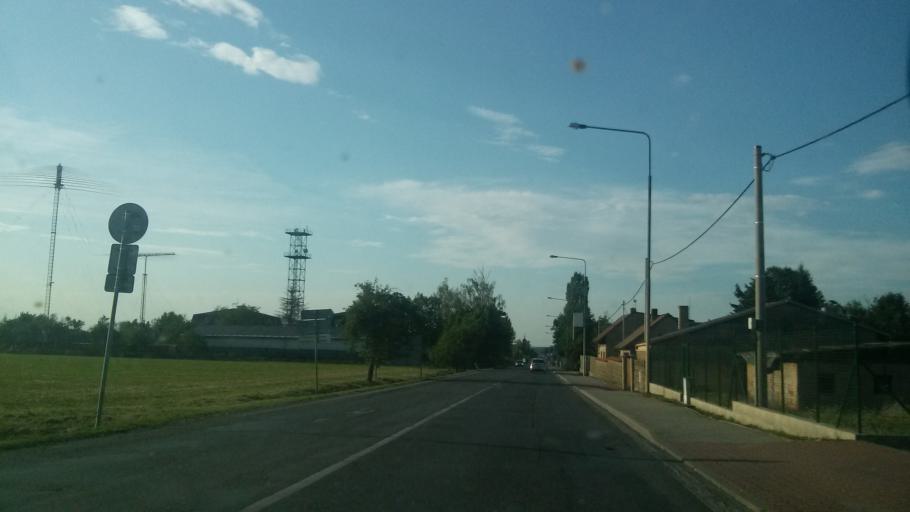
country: CZ
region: Central Bohemia
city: Vestec
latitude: 49.9797
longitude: 14.4983
